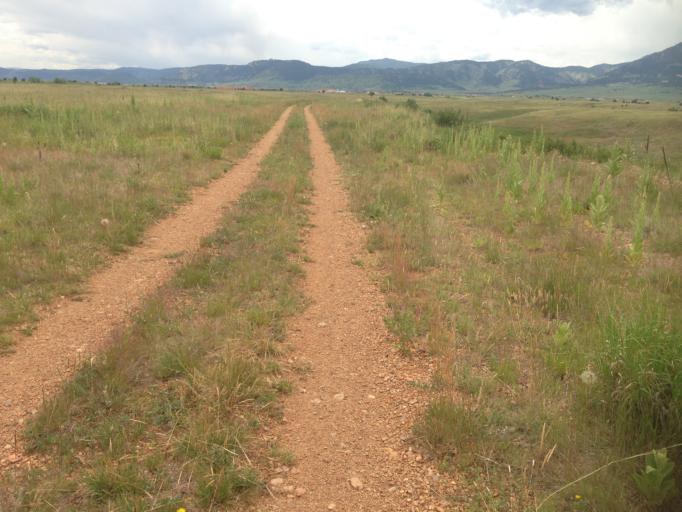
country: US
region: Colorado
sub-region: Boulder County
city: Superior
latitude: 39.9064
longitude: -105.2036
